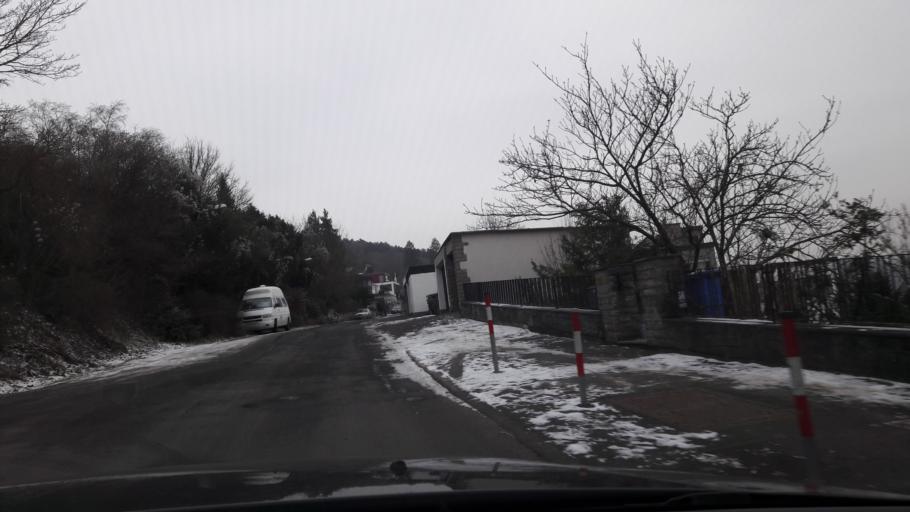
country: DE
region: Bavaria
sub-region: Regierungsbezirk Unterfranken
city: Hochberg
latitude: 49.7905
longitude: 9.9005
